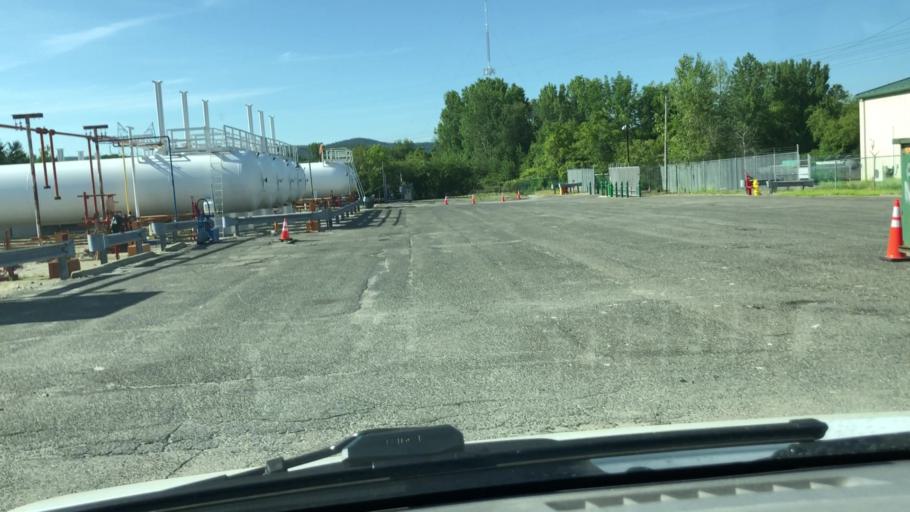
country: US
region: Massachusetts
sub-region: Berkshire County
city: Pittsfield
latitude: 42.4534
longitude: -73.2142
